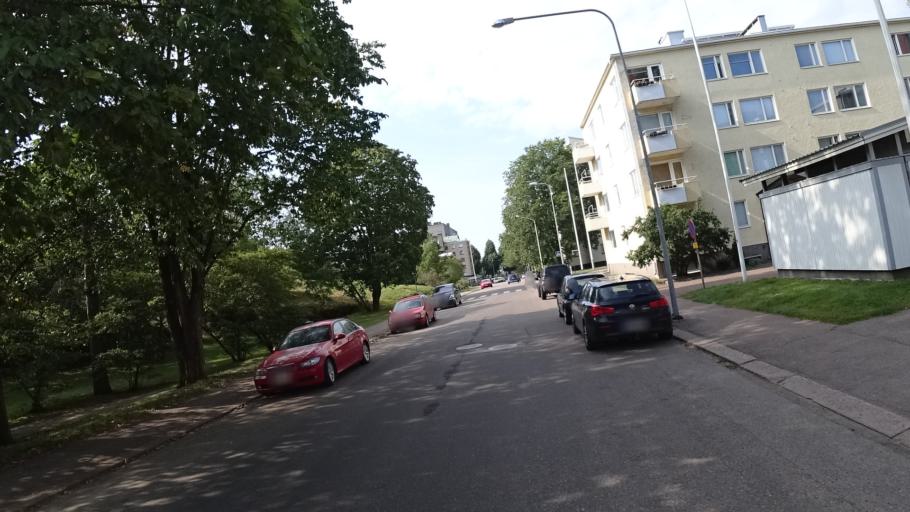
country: FI
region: Kymenlaakso
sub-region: Kotka-Hamina
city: Kotka
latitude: 60.4659
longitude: 26.9507
